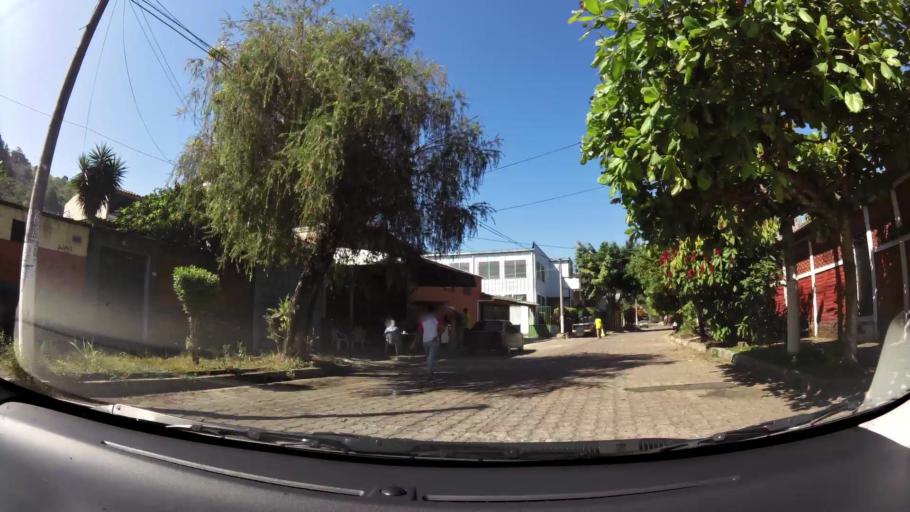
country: SV
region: La Libertad
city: Santa Tecla
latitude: 13.6675
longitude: -89.2851
